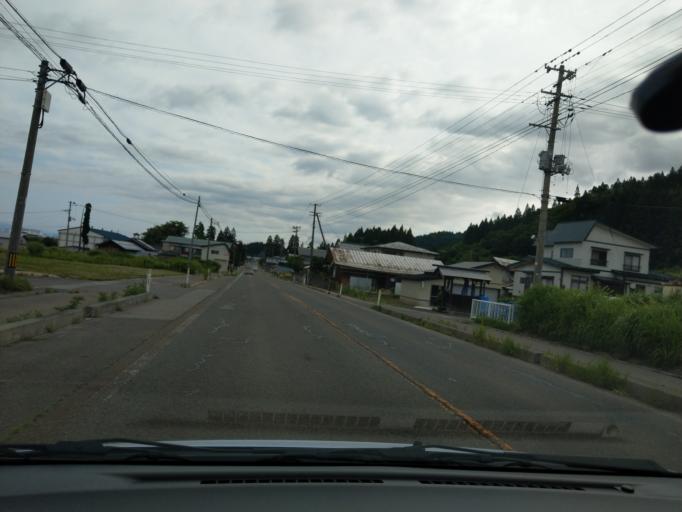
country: JP
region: Akita
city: Yokotemachi
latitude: 39.3649
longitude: 140.5663
